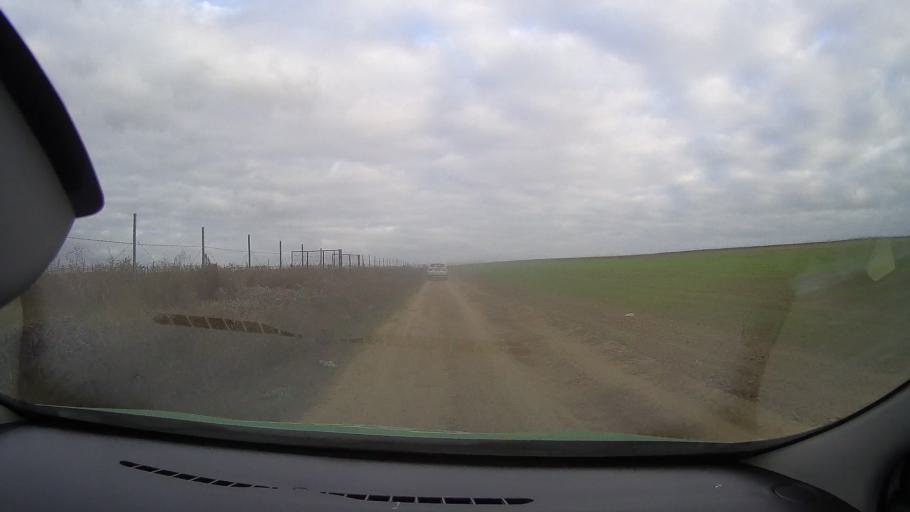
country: RO
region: Tulcea
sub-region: Comuna Jurilovca
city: Jurilovca
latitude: 44.7677
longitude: 28.9068
